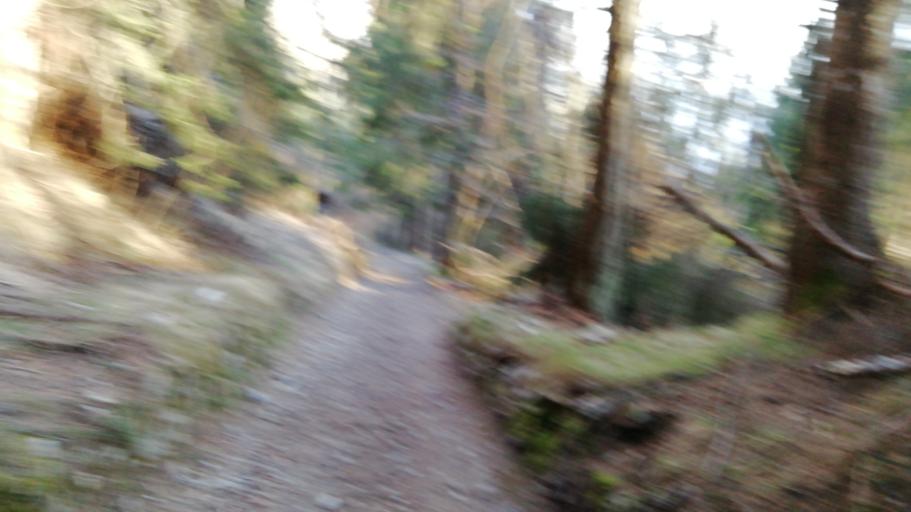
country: IT
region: Veneto
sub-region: Provincia di Belluno
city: Valle di Cadore
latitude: 46.4191
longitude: 12.3209
